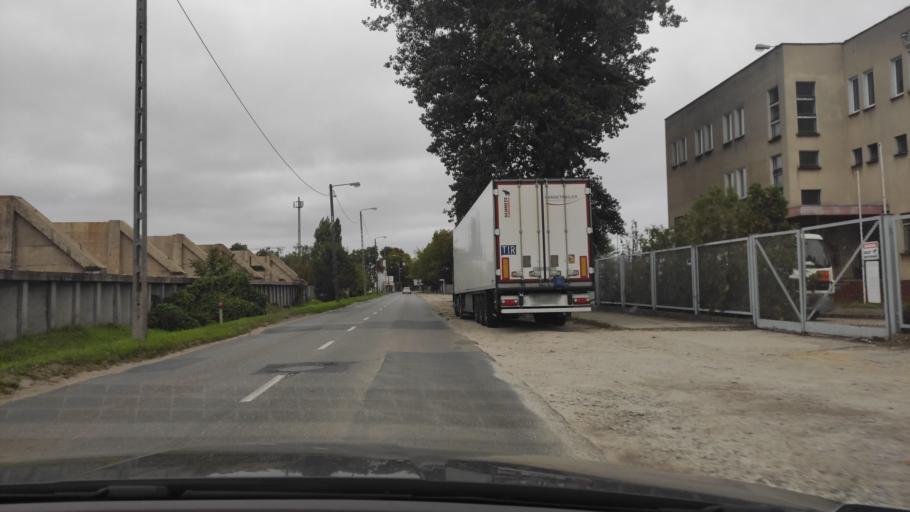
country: PL
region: Greater Poland Voivodeship
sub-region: Poznan
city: Poznan
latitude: 52.4164
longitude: 16.9754
